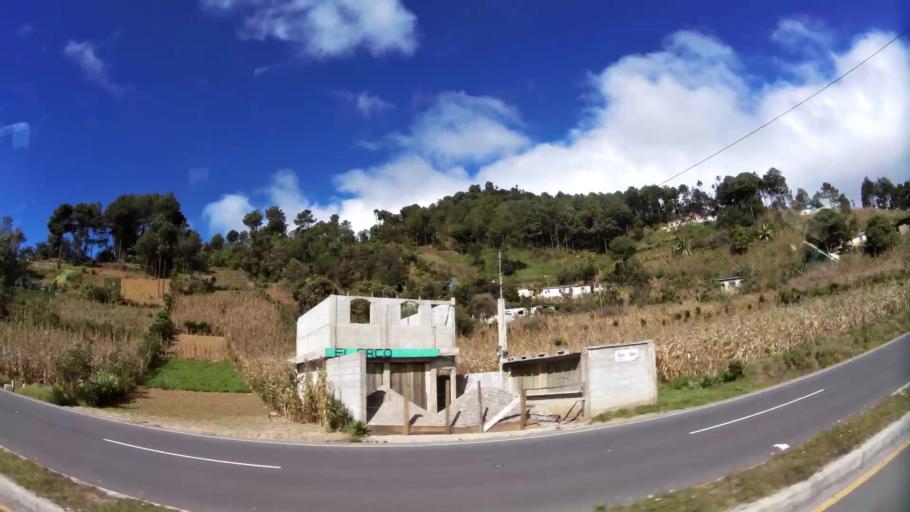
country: GT
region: Solola
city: Concepcion
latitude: 14.8378
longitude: -91.1772
